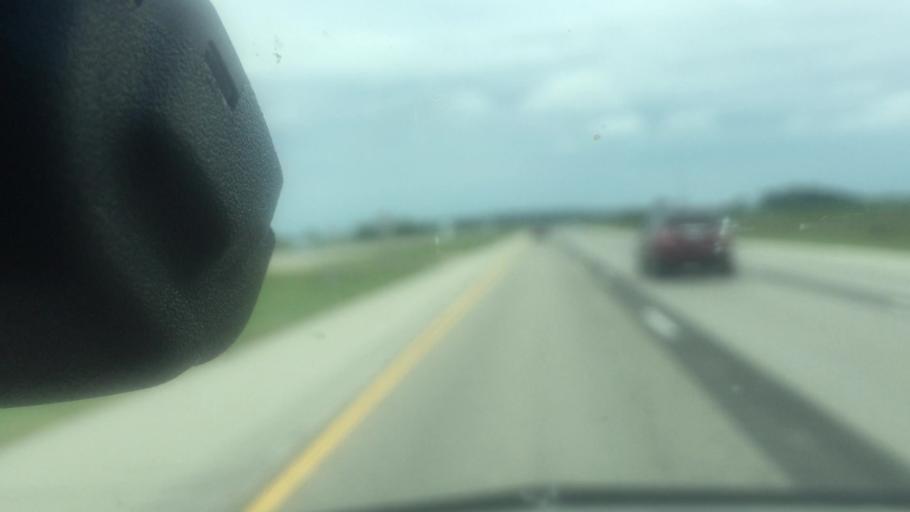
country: US
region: Illinois
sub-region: Logan County
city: Lincoln
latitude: 40.0628
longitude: -89.4494
